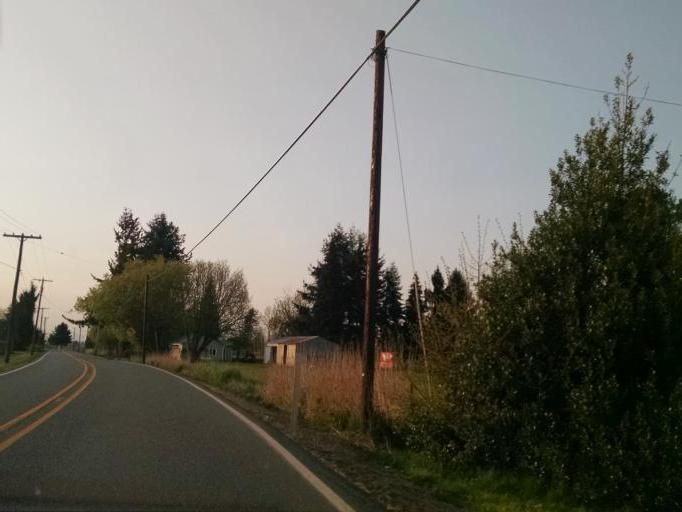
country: US
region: Washington
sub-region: Whatcom County
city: Nooksack
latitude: 48.8608
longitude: -122.3005
